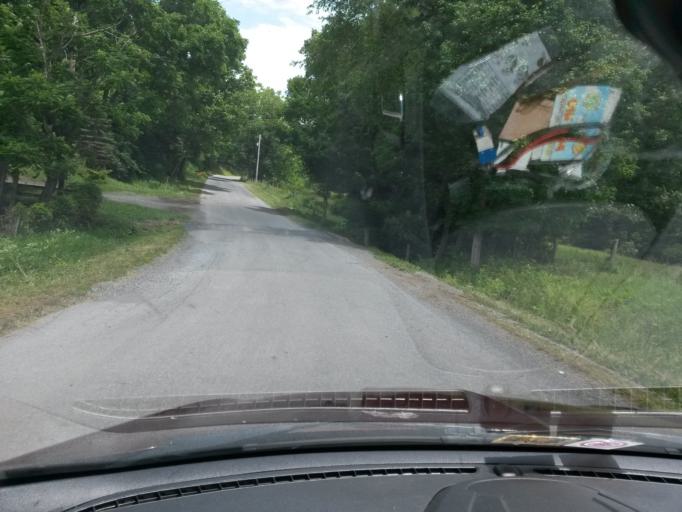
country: US
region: West Virginia
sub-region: Monroe County
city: Union
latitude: 37.5235
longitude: -80.5534
